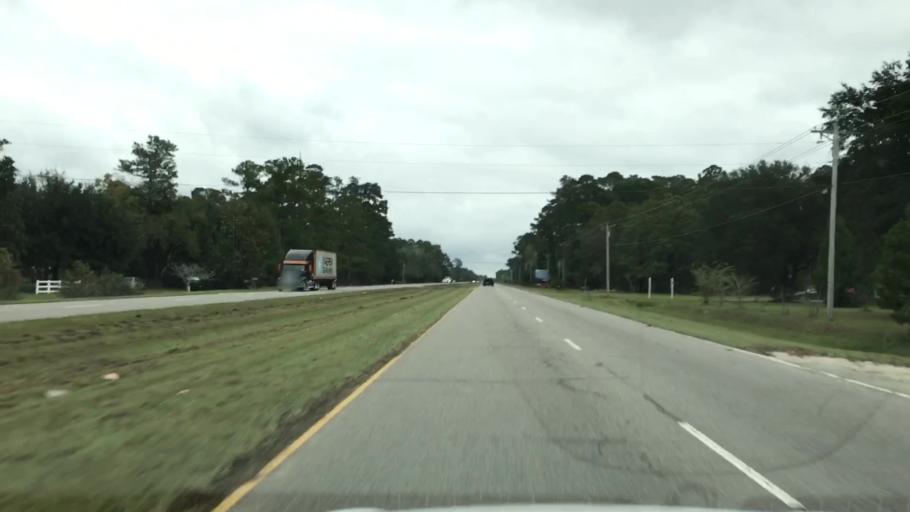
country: US
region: South Carolina
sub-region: Georgetown County
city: Georgetown
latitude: 33.3106
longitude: -79.3315
